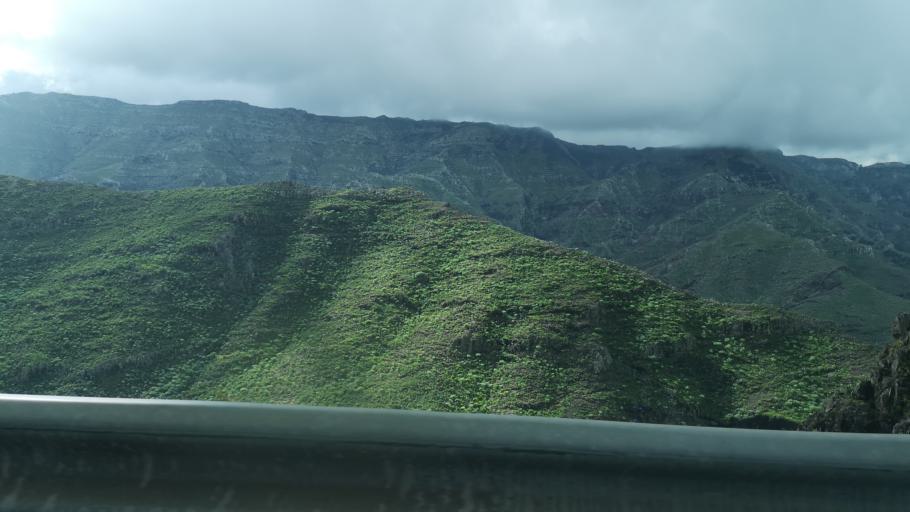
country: ES
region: Canary Islands
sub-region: Provincia de Santa Cruz de Tenerife
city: San Sebastian de la Gomera
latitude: 28.1223
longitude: -17.1527
